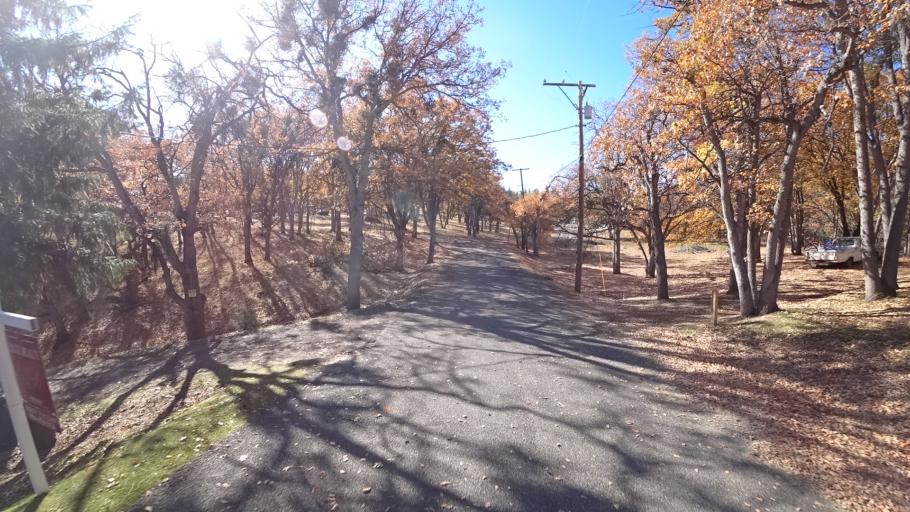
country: US
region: California
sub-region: Siskiyou County
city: Montague
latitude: 41.9794
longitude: -122.3251
